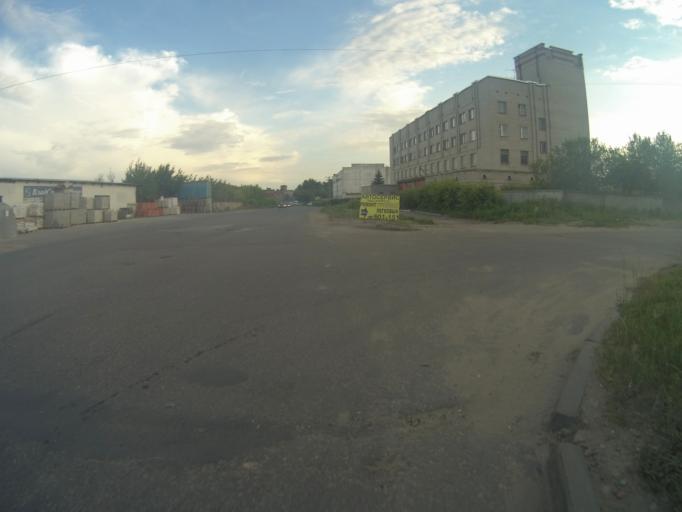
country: RU
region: Vladimir
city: Vladimir
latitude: 56.1559
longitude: 40.3828
